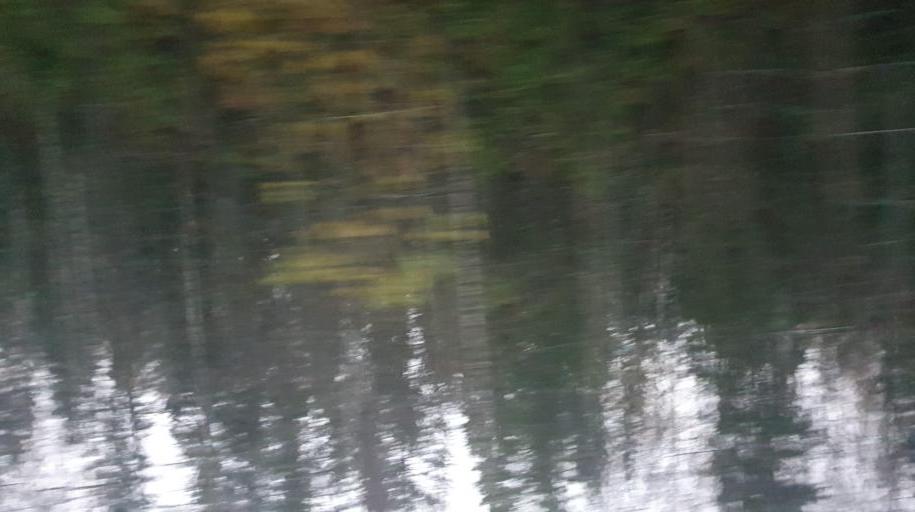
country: NO
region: Buskerud
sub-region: Krodsherad
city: Noresund
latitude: 60.1958
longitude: 9.5906
